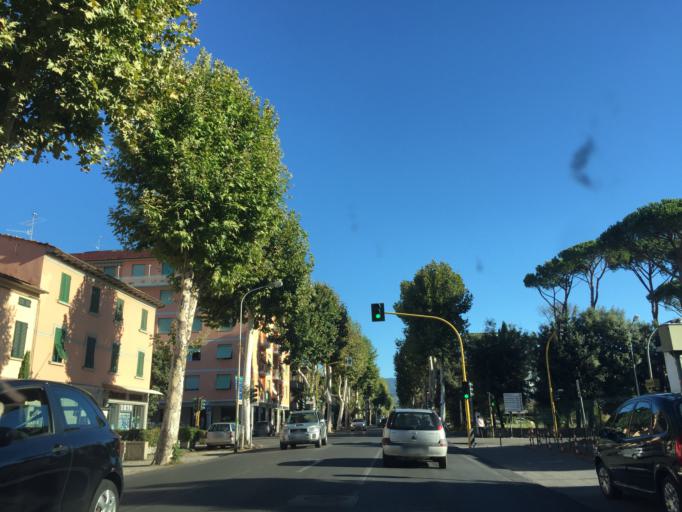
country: IT
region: Tuscany
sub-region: Provincia di Pistoia
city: Pistoia
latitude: 43.9311
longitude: 10.9005
